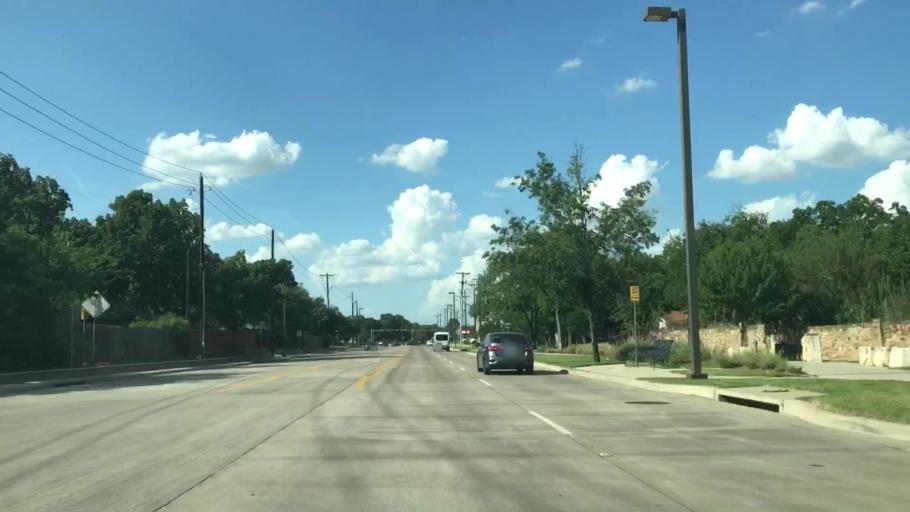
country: US
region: Texas
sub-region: Dallas County
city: Irving
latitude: 32.8550
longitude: -96.9605
